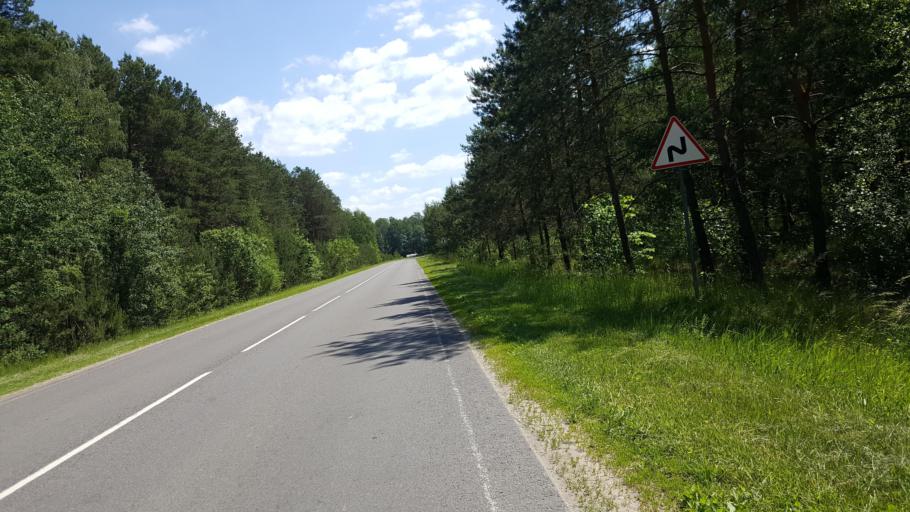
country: BY
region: Brest
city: Zhabinka
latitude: 52.2026
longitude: 24.0522
